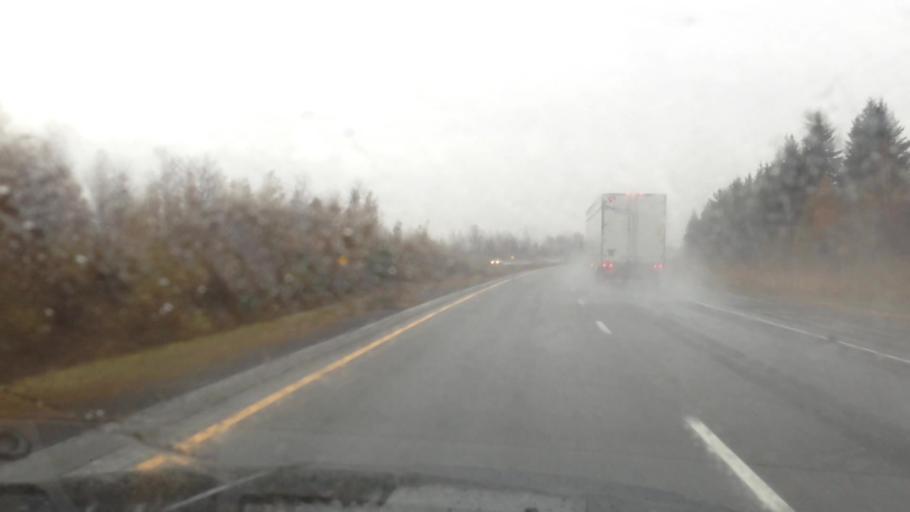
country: CA
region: Ontario
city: Casselman
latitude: 45.3149
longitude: -75.1586
